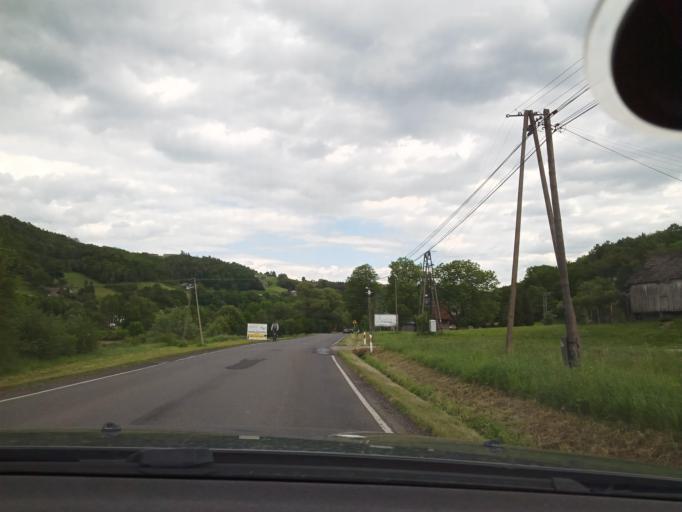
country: PL
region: Lesser Poland Voivodeship
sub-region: Powiat limanowski
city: Tymbark
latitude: 49.7503
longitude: 20.3589
